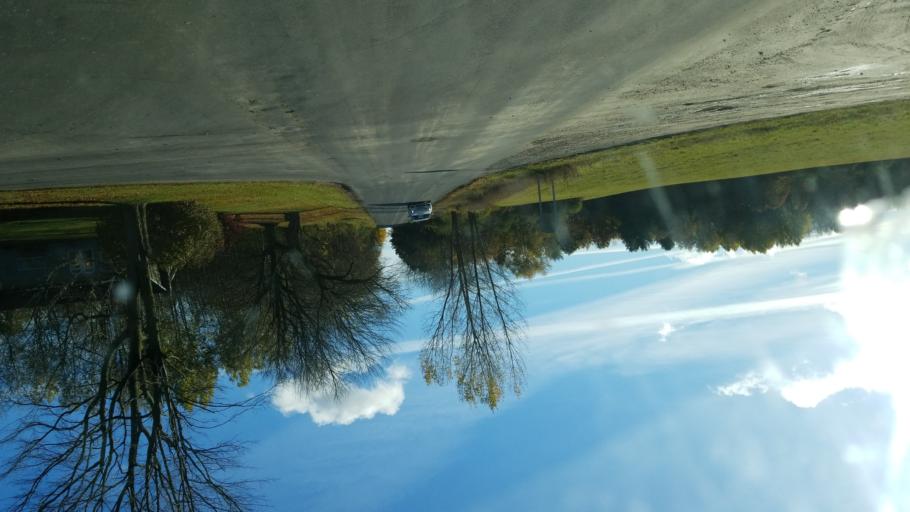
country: US
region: Michigan
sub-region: Montcalm County
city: Edmore
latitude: 43.4297
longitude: -85.1046
